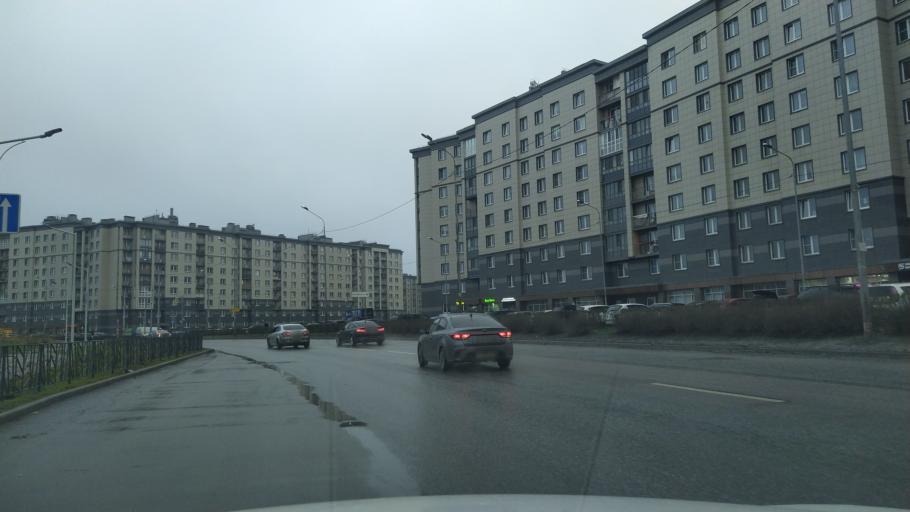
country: RU
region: St.-Petersburg
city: Tyarlevo
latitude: 59.7420
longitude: 30.4707
